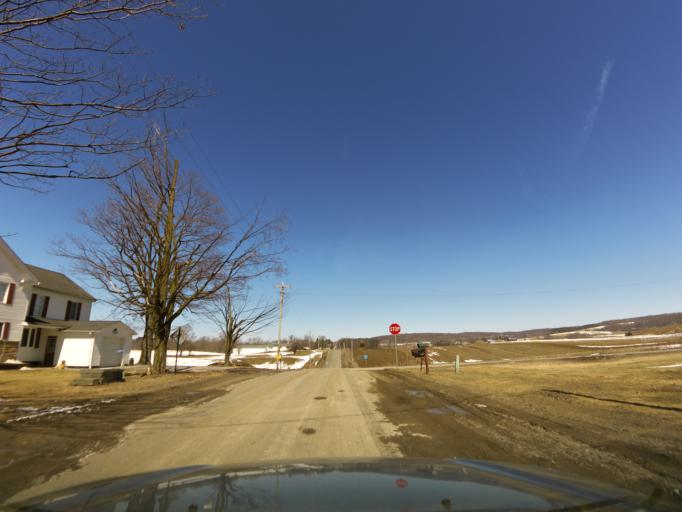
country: US
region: New York
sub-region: Cattaraugus County
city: Delevan
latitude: 42.4409
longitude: -78.4282
